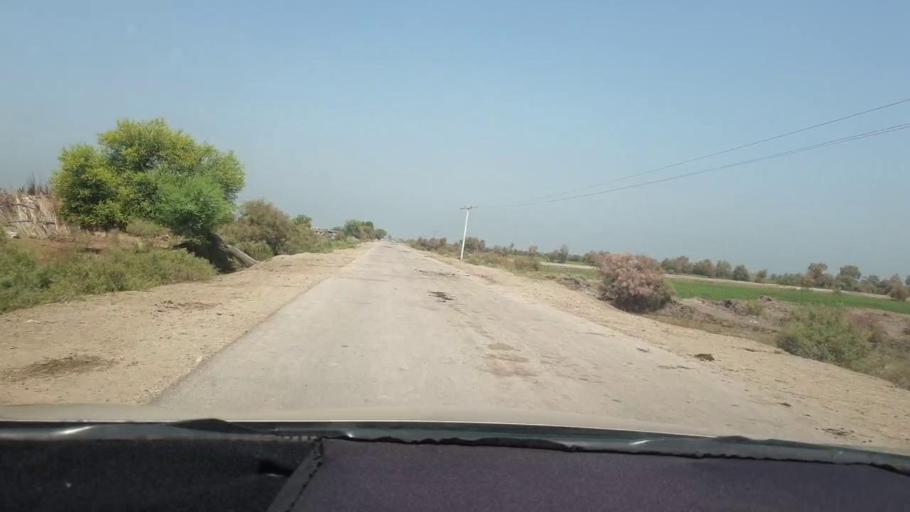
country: PK
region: Sindh
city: Miro Khan
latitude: 27.8257
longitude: 68.0192
